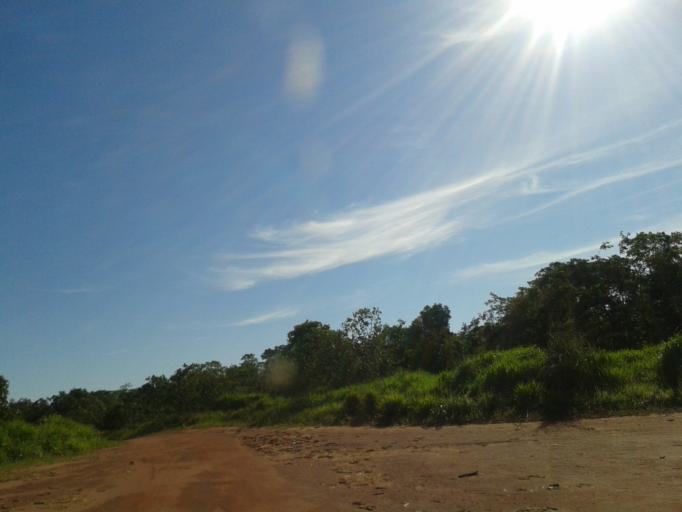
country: BR
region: Minas Gerais
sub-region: Santa Vitoria
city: Santa Vitoria
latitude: -19.1176
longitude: -49.9924
